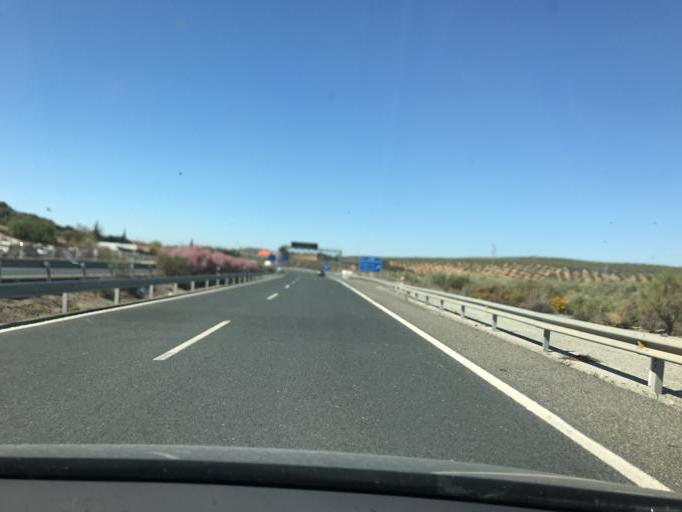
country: ES
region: Andalusia
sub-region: Provincia de Malaga
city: Villanueva de Tapia
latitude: 37.1370
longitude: -4.2810
